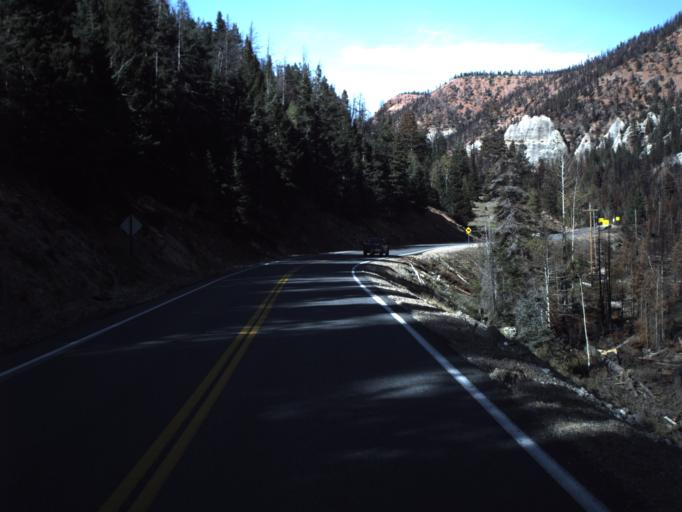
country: US
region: Utah
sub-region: Iron County
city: Parowan
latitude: 37.7270
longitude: -112.8405
